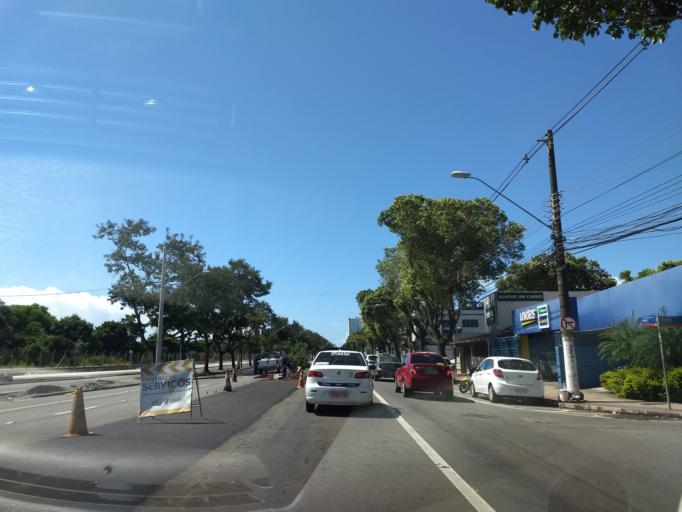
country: BR
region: Espirito Santo
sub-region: Vila Velha
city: Vila Velha
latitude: -20.2674
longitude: -40.2947
